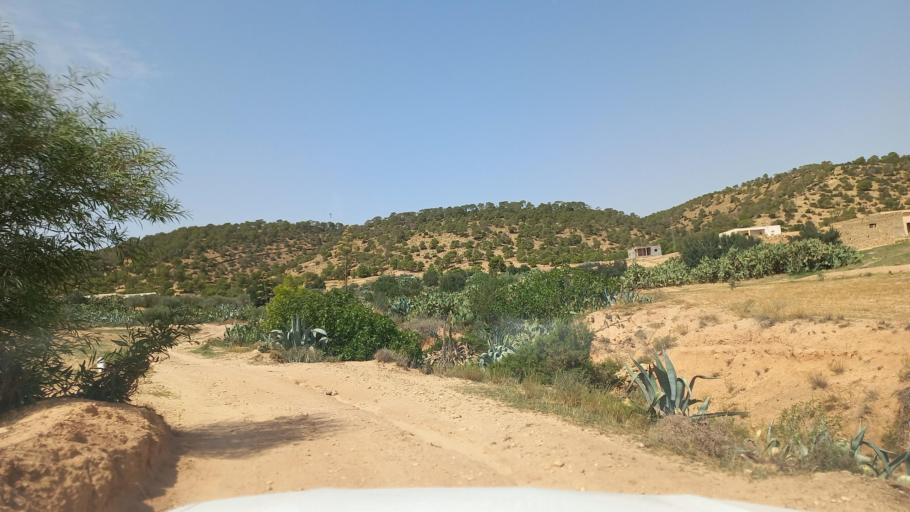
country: TN
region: Al Qasrayn
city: Kasserine
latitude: 35.3784
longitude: 8.9128
